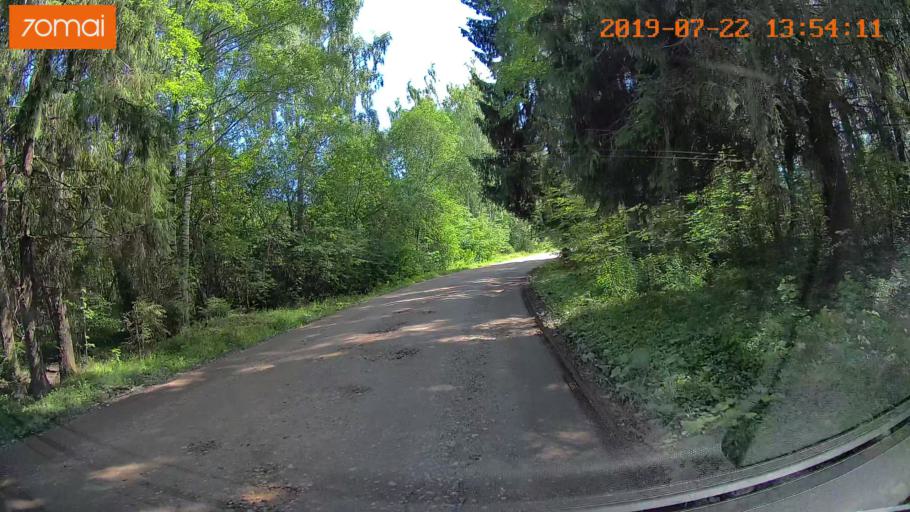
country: RU
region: Ivanovo
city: Novo-Talitsy
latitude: 57.0791
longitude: 40.8797
